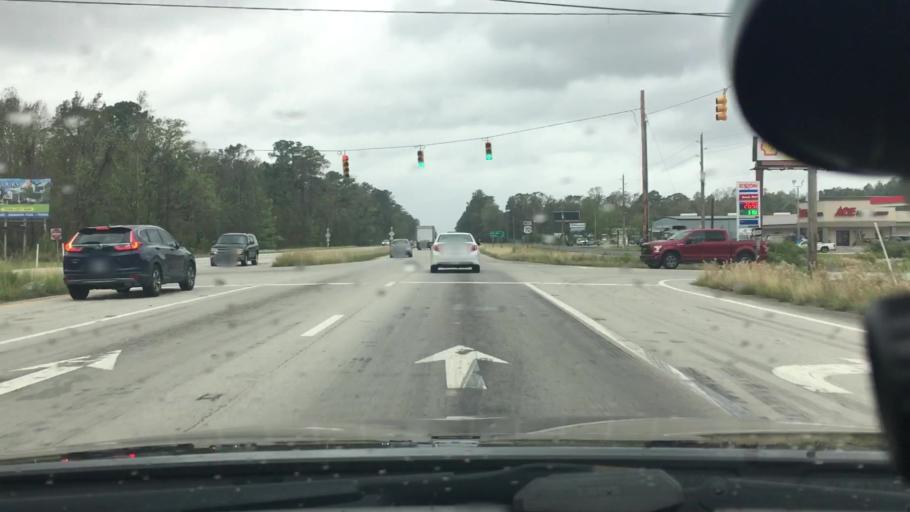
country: US
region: North Carolina
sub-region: Craven County
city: James City
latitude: 35.0378
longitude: -77.0070
